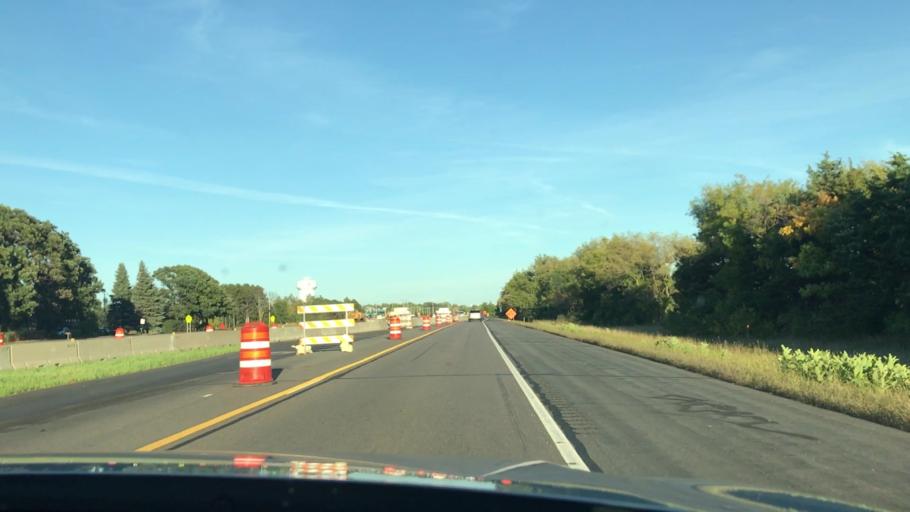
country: US
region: Minnesota
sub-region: Wright County
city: Otsego
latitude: 45.3060
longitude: -93.6165
